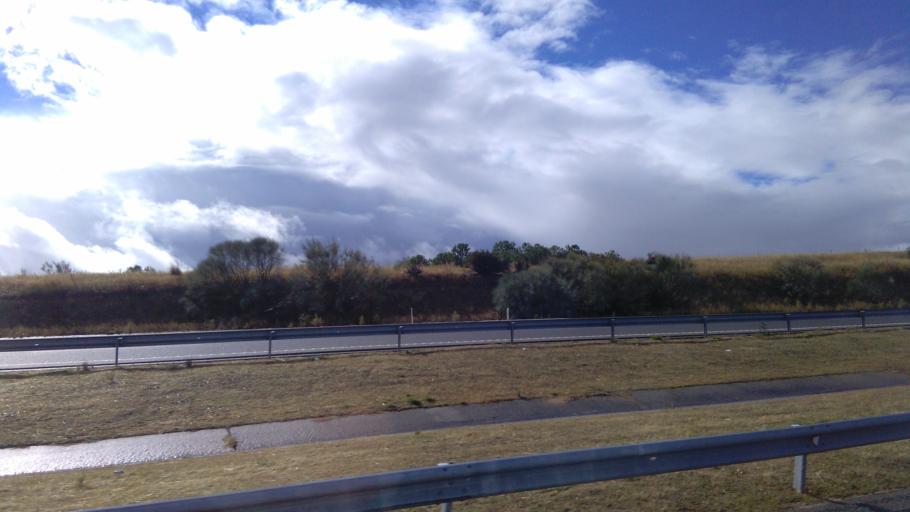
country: ES
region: Madrid
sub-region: Provincia de Madrid
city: Navalcarnero
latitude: 40.2655
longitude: -4.0212
